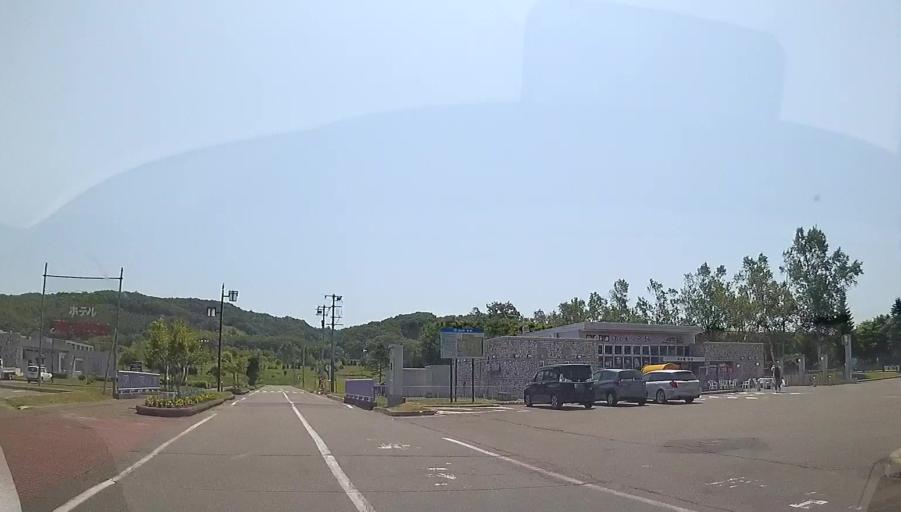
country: JP
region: Hokkaido
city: Obihiro
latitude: 42.5593
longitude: 143.2989
